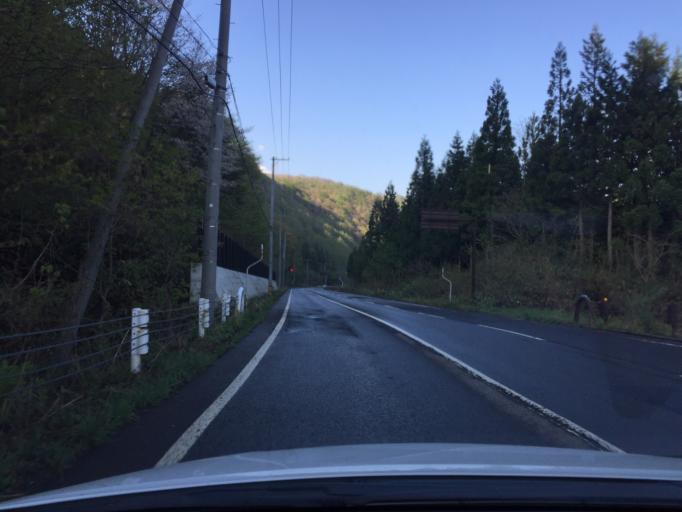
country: JP
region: Fukushima
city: Inawashiro
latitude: 37.6639
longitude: 140.0295
